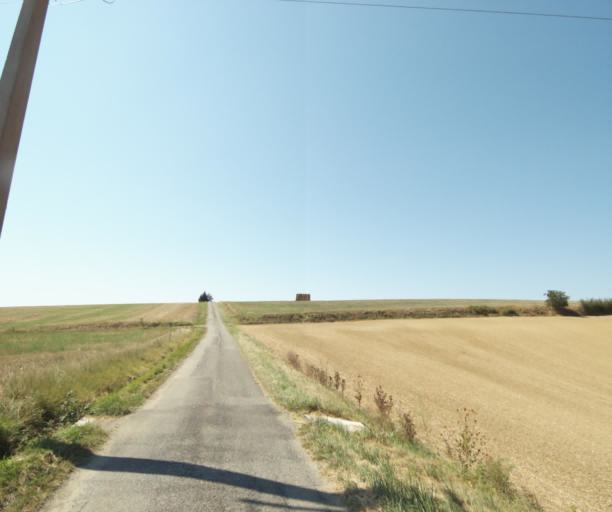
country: FR
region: Midi-Pyrenees
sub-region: Departement de l'Ariege
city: Lezat-sur-Leze
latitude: 43.2707
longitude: 1.3760
